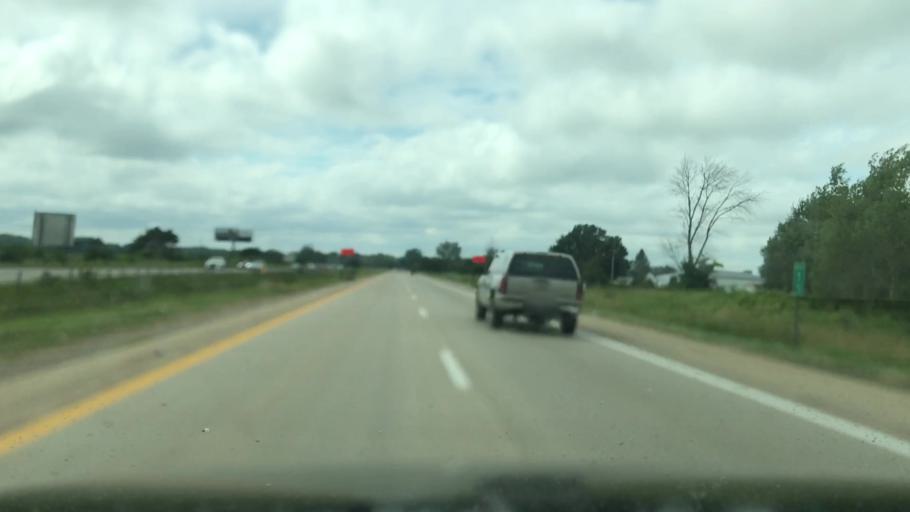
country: US
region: Michigan
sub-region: Ottawa County
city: Coopersville
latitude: 43.0648
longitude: -85.9724
